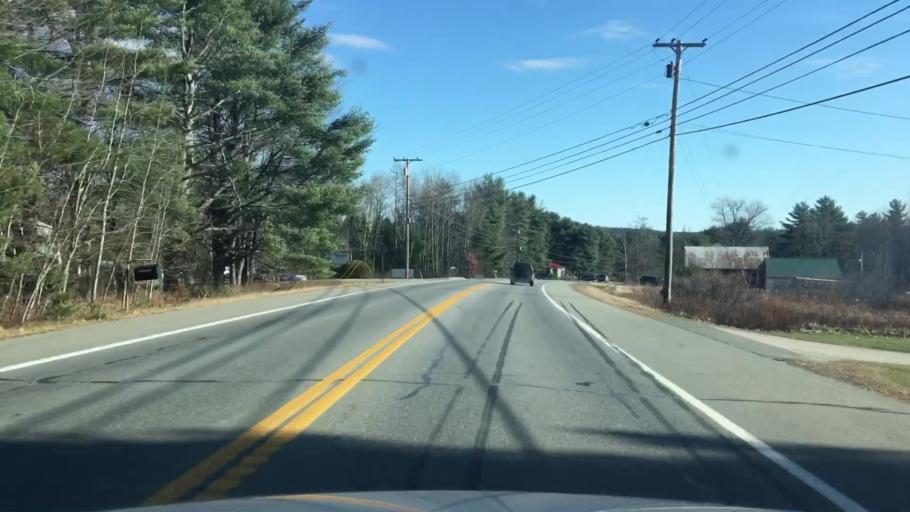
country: US
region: Maine
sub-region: Kennebec County
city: Windsor
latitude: 44.2690
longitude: -69.5708
